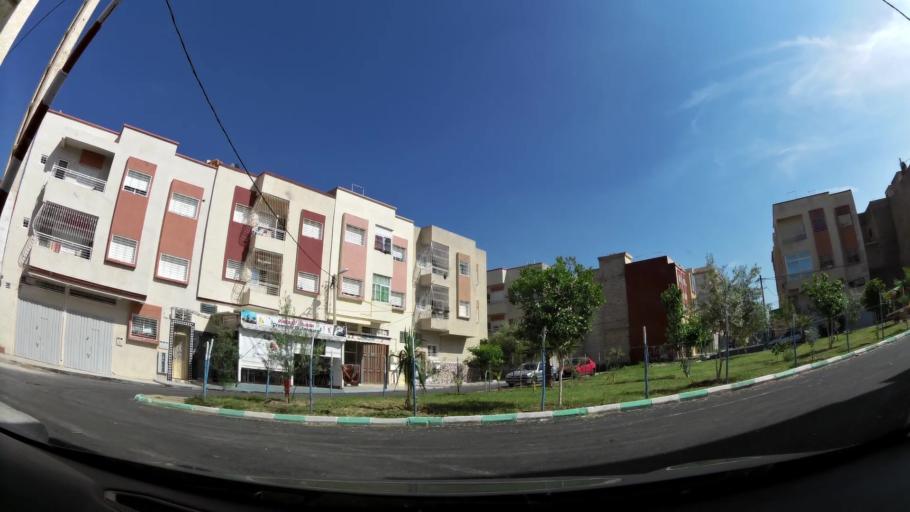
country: MA
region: Fes-Boulemane
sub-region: Fes
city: Fes
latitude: 34.0083
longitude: -5.0332
